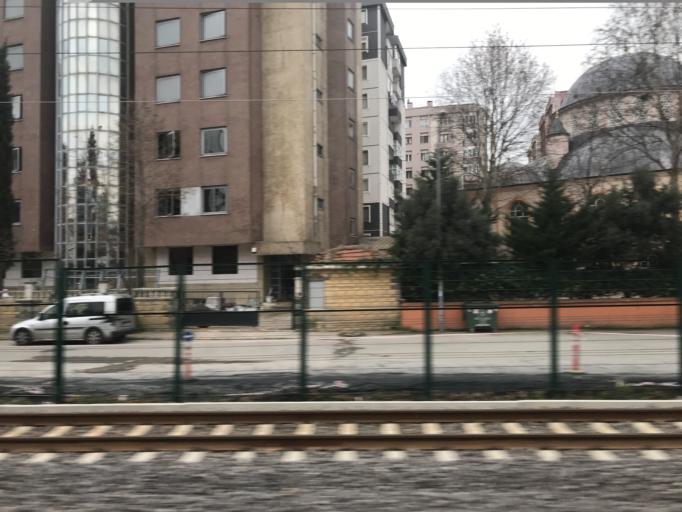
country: TR
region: Istanbul
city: Maltepe
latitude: 40.9120
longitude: 29.1539
